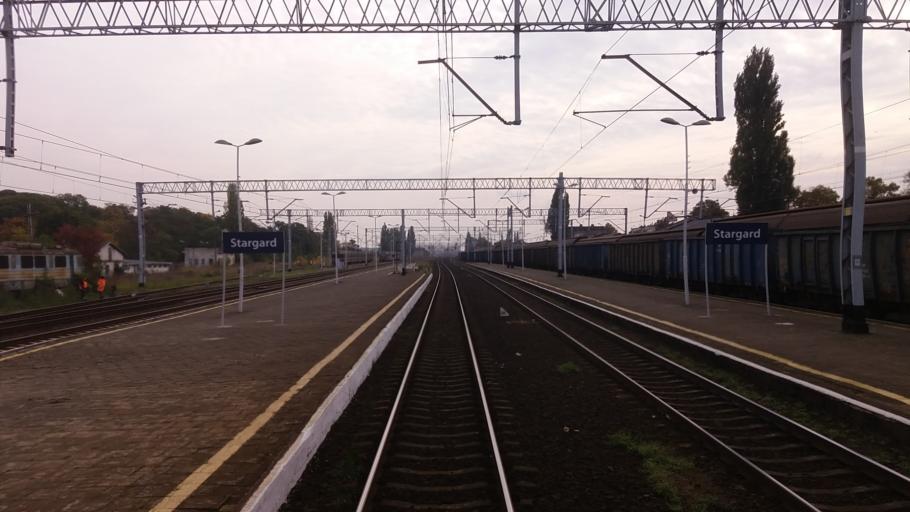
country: PL
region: West Pomeranian Voivodeship
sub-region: Powiat stargardzki
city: Stargard Szczecinski
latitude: 53.3385
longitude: 15.0319
